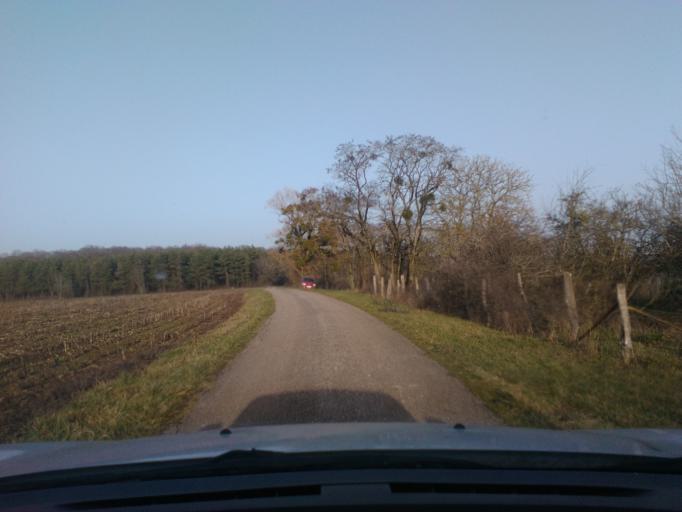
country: FR
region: Lorraine
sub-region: Departement des Vosges
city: Vittel
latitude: 48.2596
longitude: 6.0007
